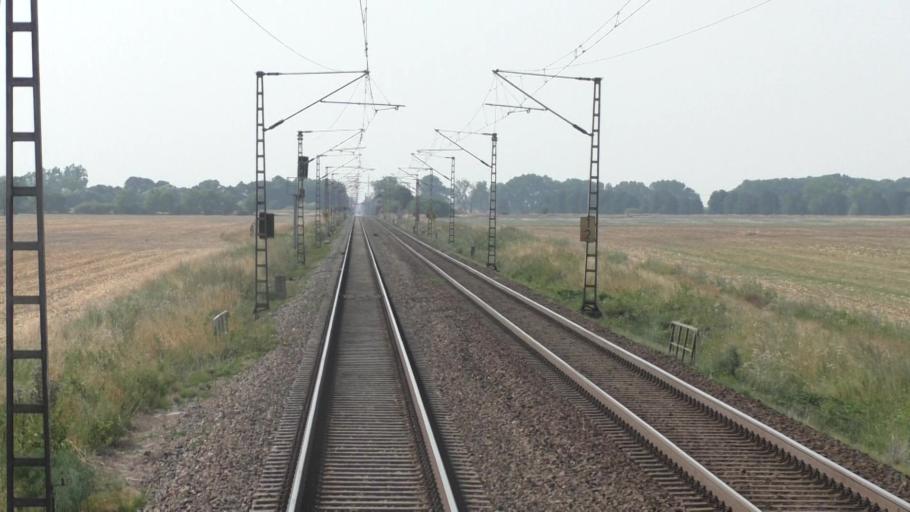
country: DE
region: Saxony-Anhalt
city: Zerbst
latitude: 51.9719
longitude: 12.0453
